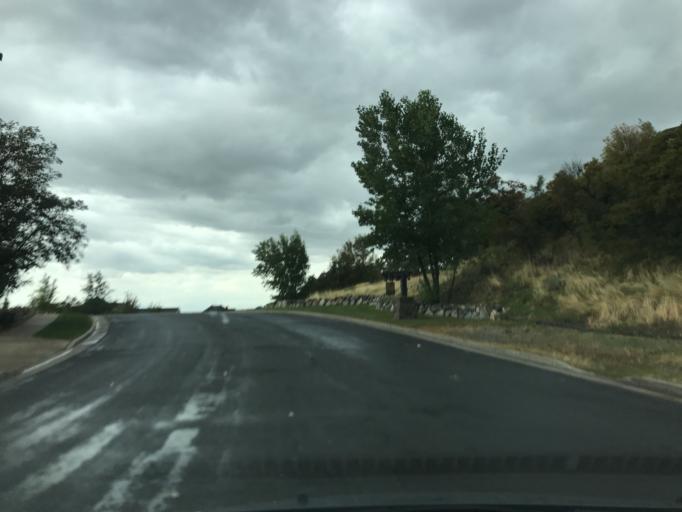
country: US
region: Utah
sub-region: Davis County
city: Fruit Heights
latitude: 41.0130
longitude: -111.8972
